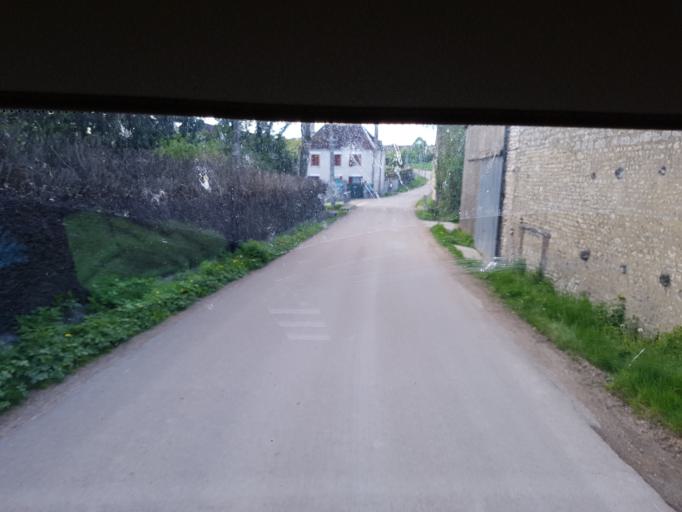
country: FR
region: Bourgogne
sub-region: Departement de l'Yonne
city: Neuvy-Sautour
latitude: 48.0532
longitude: 3.7726
